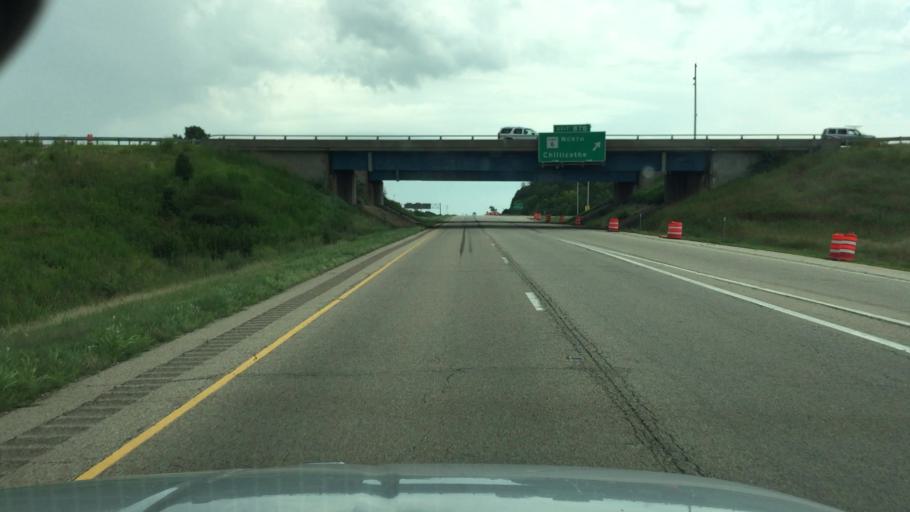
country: US
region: Illinois
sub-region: Peoria County
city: Bellevue
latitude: 40.7417
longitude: -89.6688
